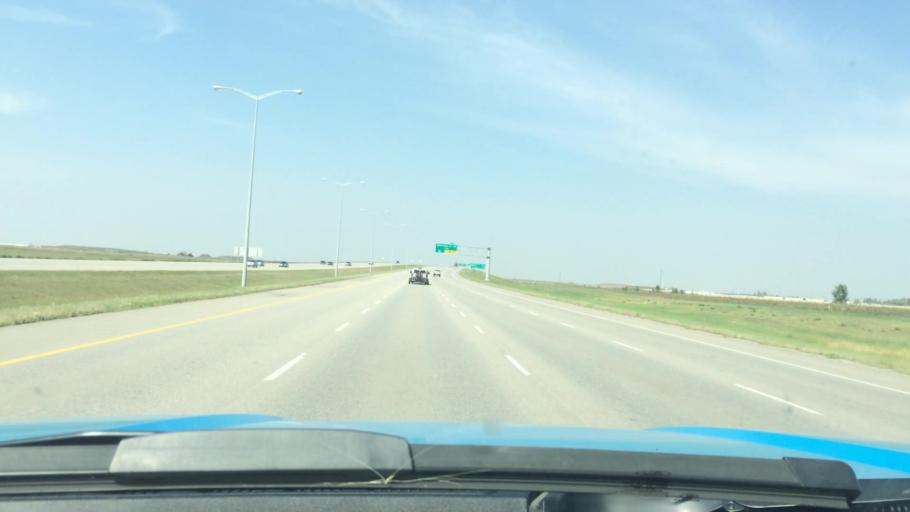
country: CA
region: Alberta
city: Chestermere
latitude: 50.9635
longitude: -113.9206
